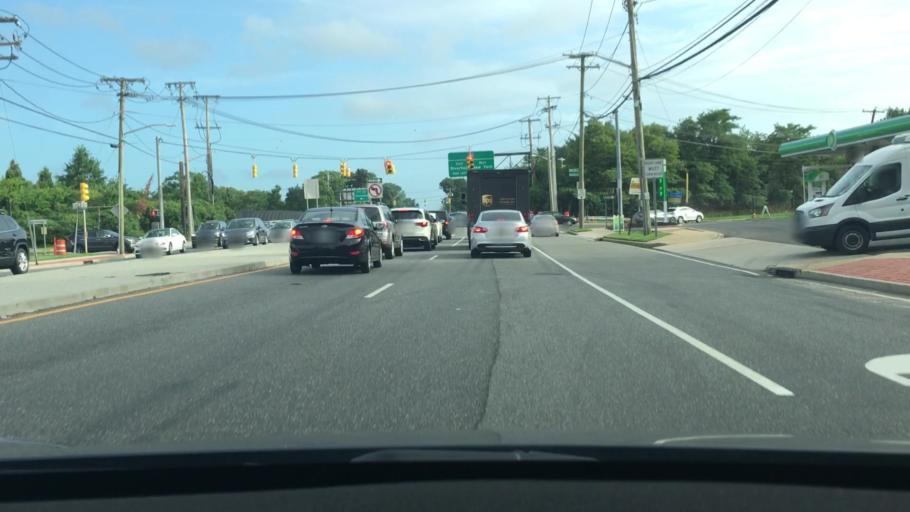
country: US
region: New York
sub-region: Nassau County
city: Syosset
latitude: 40.7988
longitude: -73.5029
